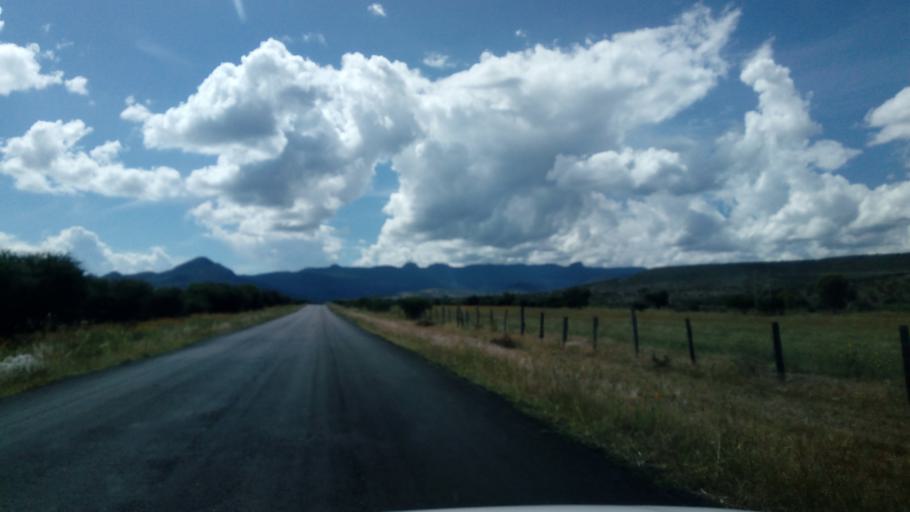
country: MX
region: Durango
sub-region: Durango
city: Jose Refugio Salcido
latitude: 23.8087
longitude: -104.4840
